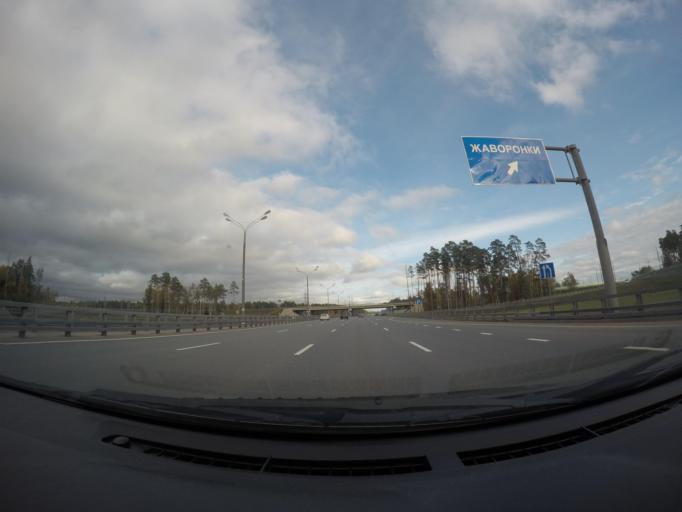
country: RU
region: Moskovskaya
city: Zhavoronki
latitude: 55.6159
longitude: 37.0946
